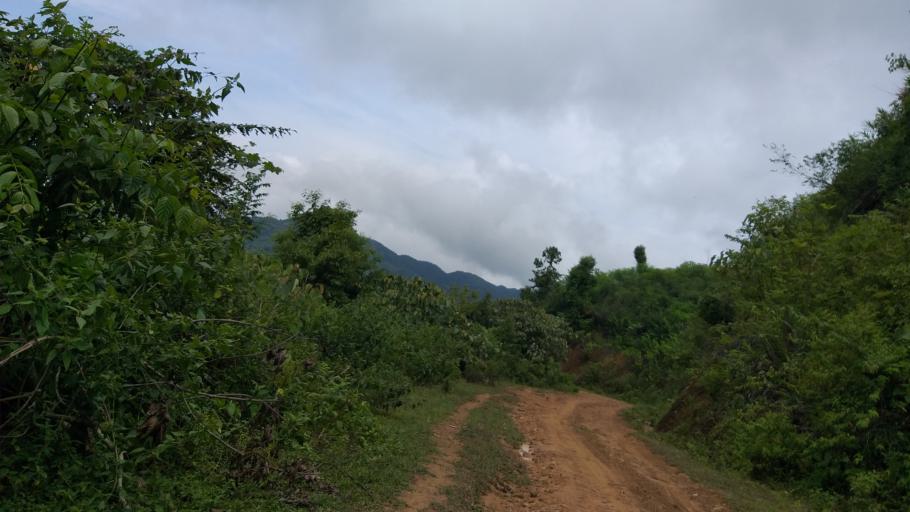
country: LA
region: Phongsali
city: Khoa
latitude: 21.3941
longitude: 102.6664
